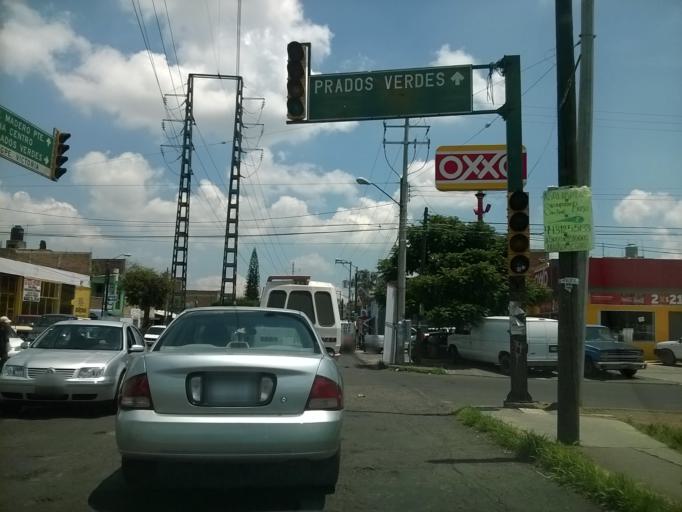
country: MX
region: Michoacan
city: Morelia
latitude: 19.7134
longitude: -101.1974
